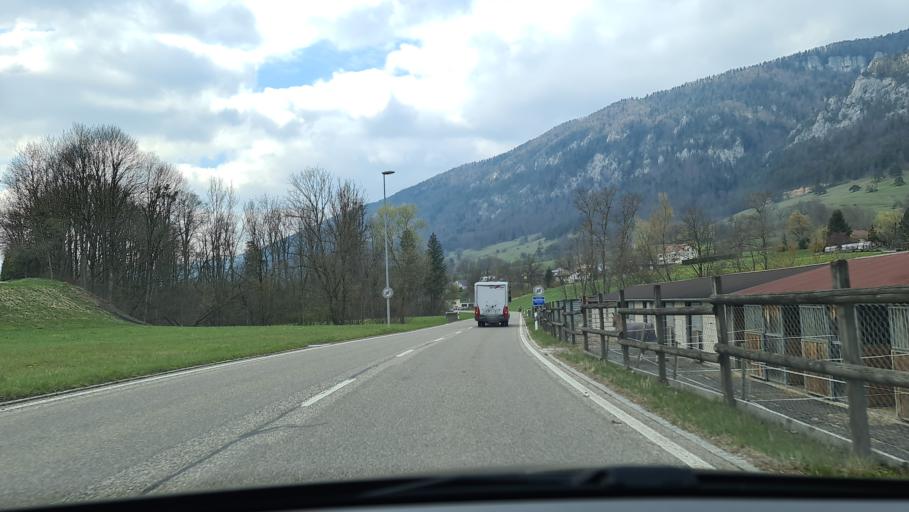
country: CH
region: Bern
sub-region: Jura bernois
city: Moutier
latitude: 47.2827
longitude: 7.4362
